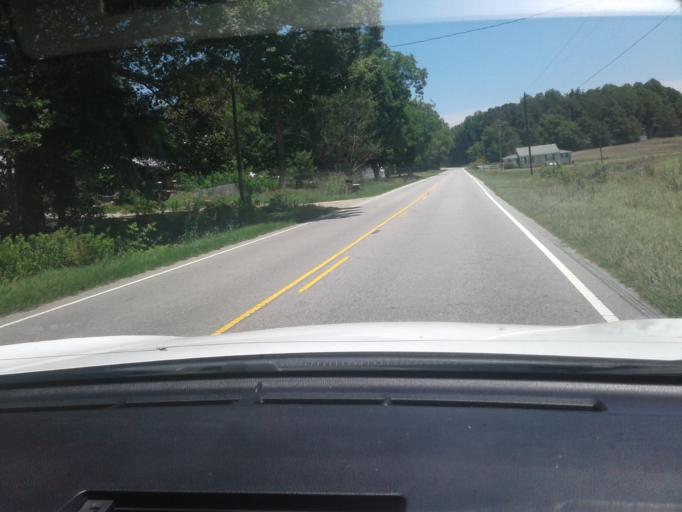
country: US
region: North Carolina
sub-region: Harnett County
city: Lillington
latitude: 35.3714
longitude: -78.8696
